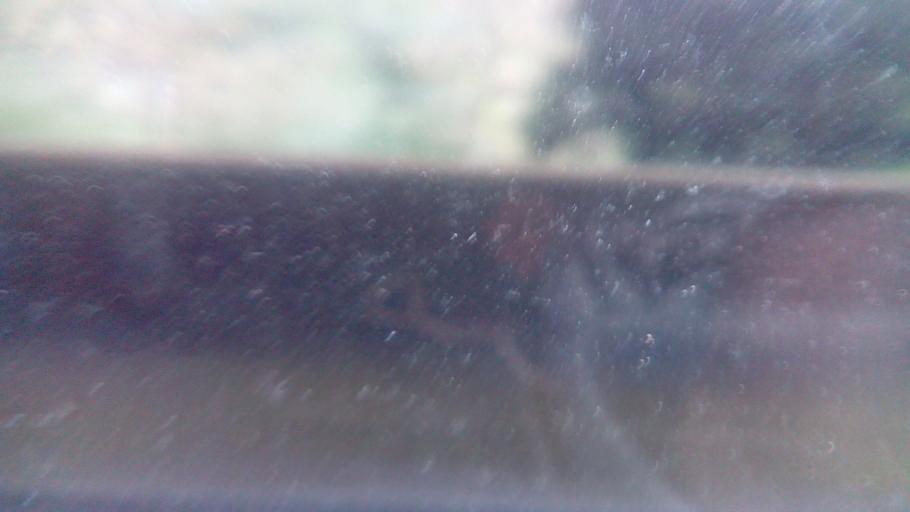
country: TW
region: Taiwan
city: Daxi
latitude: 24.4620
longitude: 121.3945
